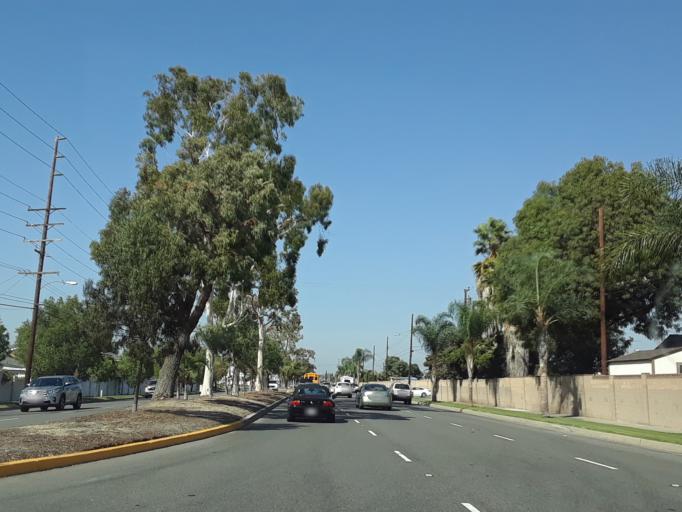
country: US
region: California
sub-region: Orange County
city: Cypress
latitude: 33.8119
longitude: -118.0282
